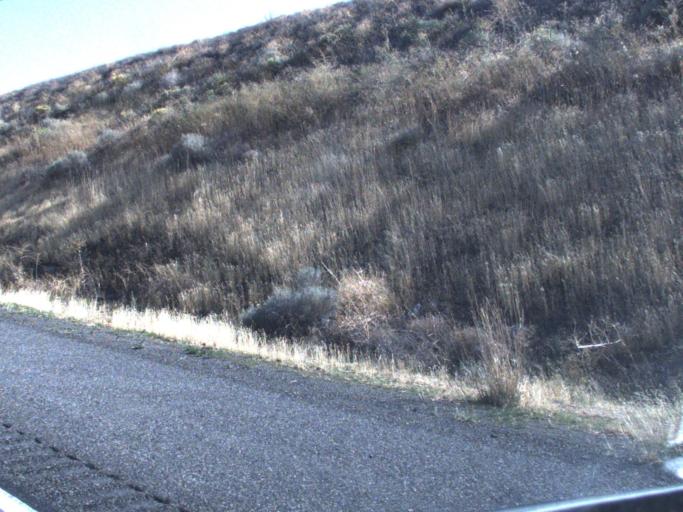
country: US
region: Washington
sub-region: Franklin County
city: West Pasco
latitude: 46.1822
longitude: -119.2442
